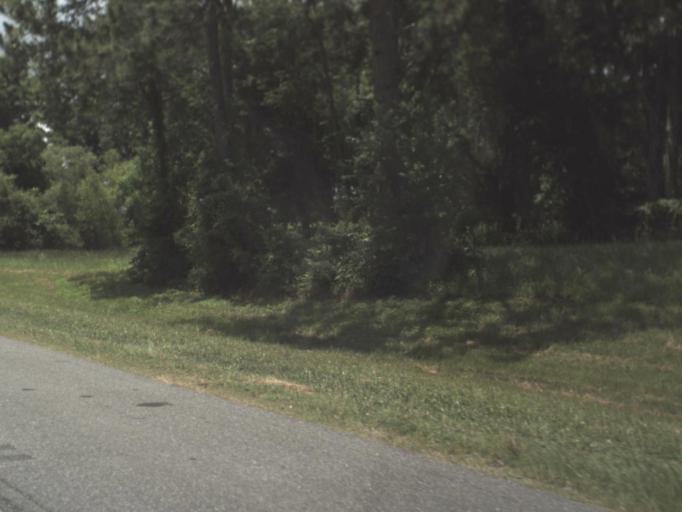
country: US
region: Florida
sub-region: Columbia County
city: Lake City
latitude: 30.1020
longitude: -82.6469
